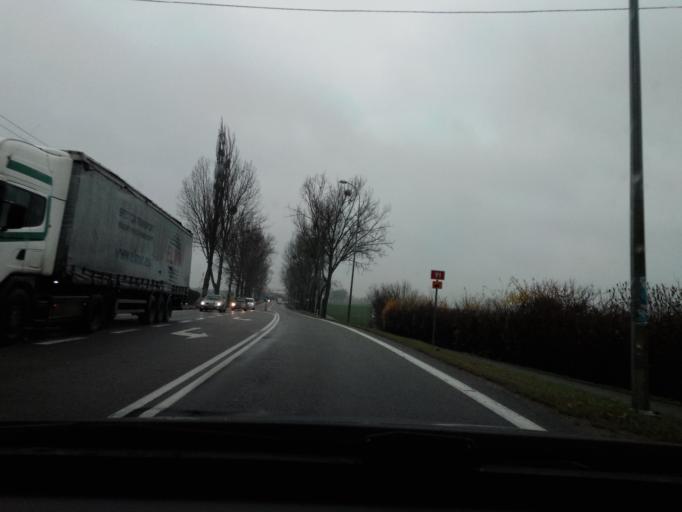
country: PL
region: Pomeranian Voivodeship
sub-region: Powiat starogardzki
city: Smetowo Graniczne
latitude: 53.7670
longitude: 18.7681
